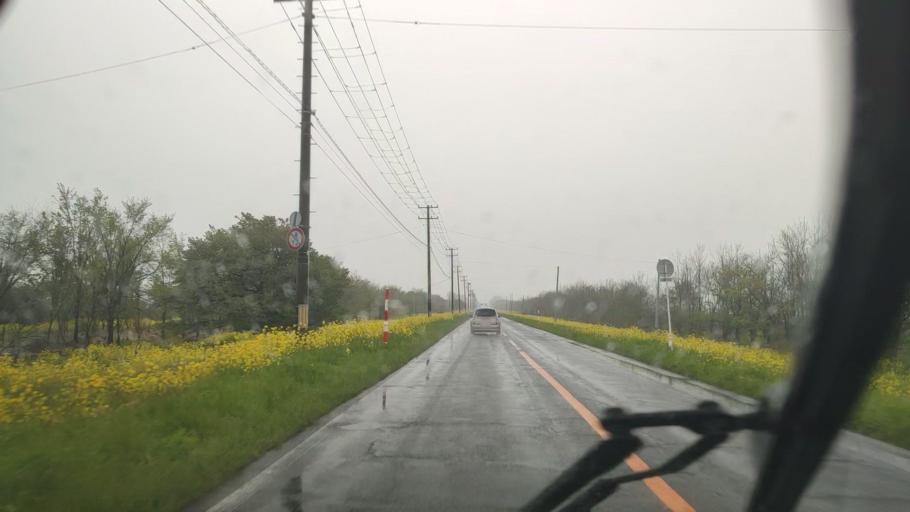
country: JP
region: Akita
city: Tenno
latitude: 39.9987
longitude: 139.9463
